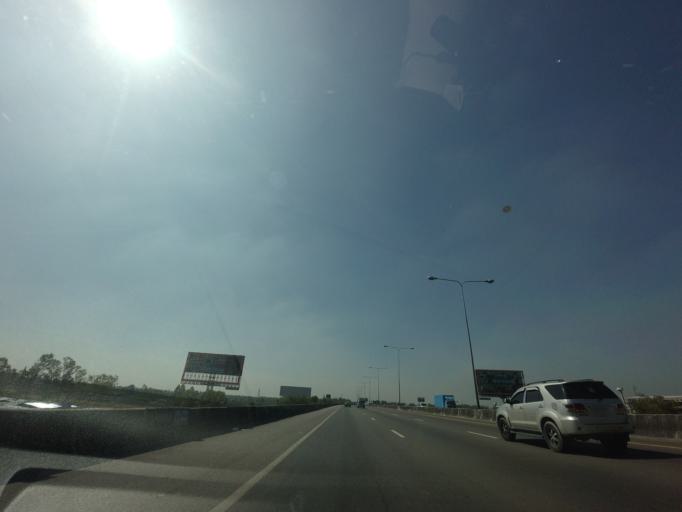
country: TH
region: Bangkok
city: Bang Na
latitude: 13.6386
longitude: 100.6786
